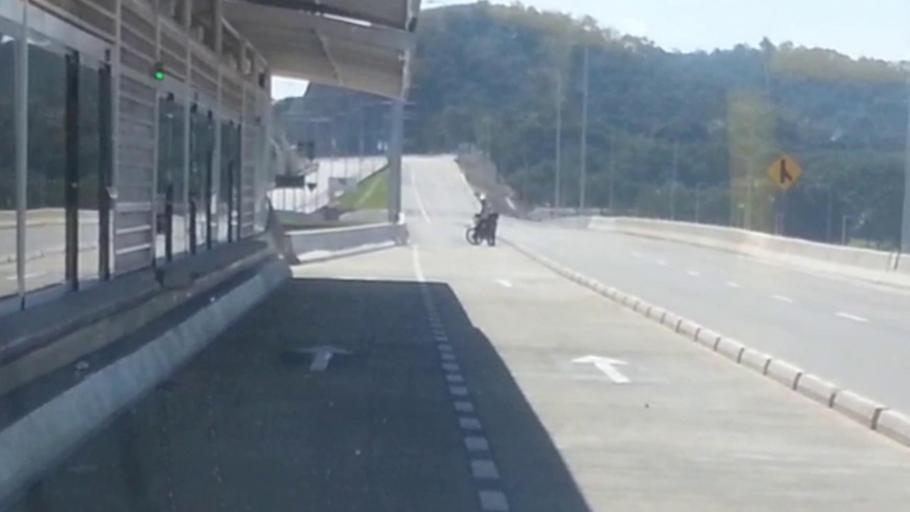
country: BR
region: Rio de Janeiro
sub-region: Nilopolis
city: Nilopolis
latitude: -22.8874
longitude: -43.4008
